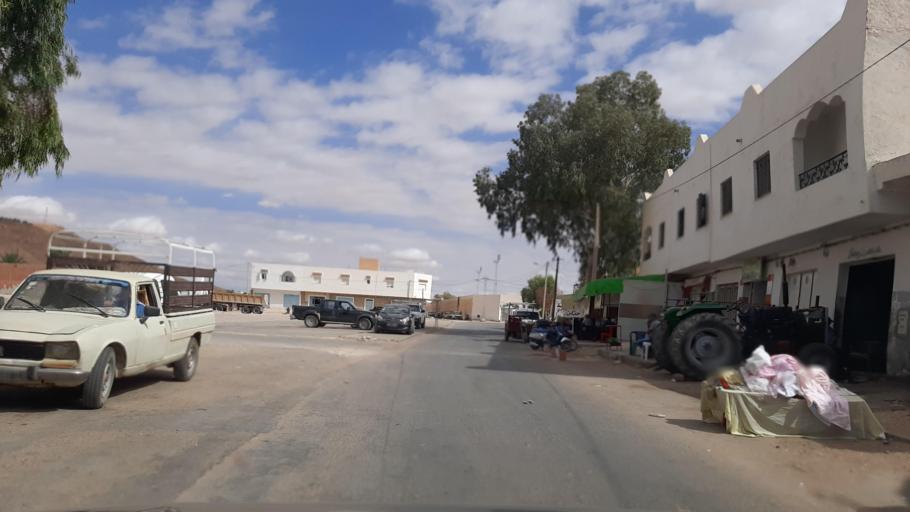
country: TN
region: Tataouine
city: Tataouine
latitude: 32.9266
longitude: 10.4410
